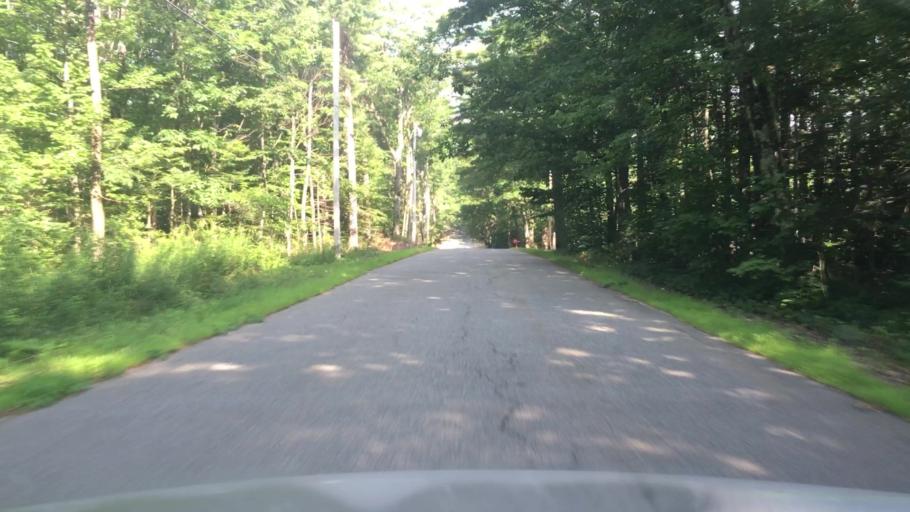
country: US
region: Maine
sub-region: Kennebec County
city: Monmouth
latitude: 44.2361
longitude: -70.0720
